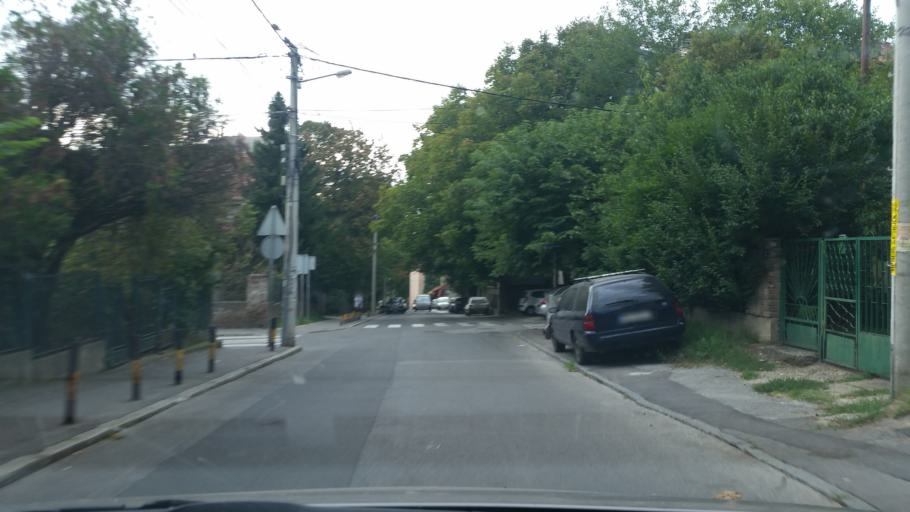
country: RS
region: Central Serbia
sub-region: Belgrade
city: Palilula
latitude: 44.8058
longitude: 20.4967
